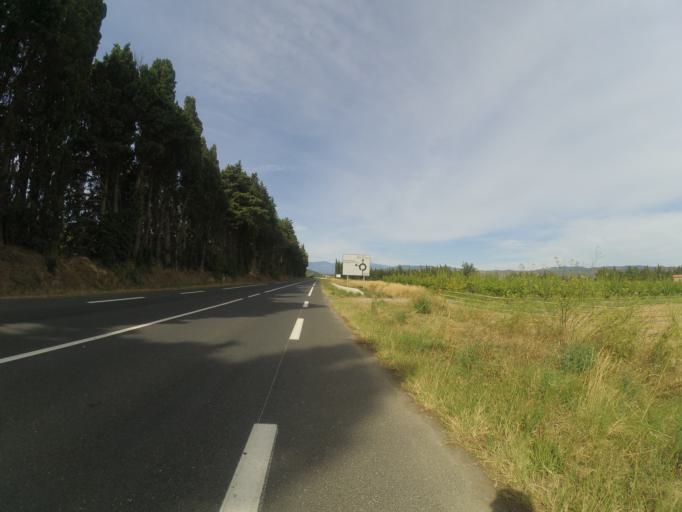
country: FR
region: Languedoc-Roussillon
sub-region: Departement des Pyrenees-Orientales
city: Ille-sur-Tet
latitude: 42.6583
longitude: 2.6450
